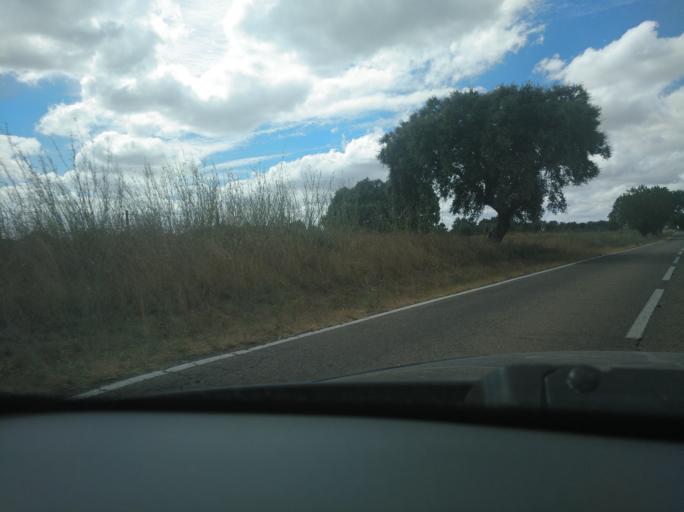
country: PT
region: Portalegre
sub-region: Arronches
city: Arronches
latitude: 39.0443
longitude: -7.4281
